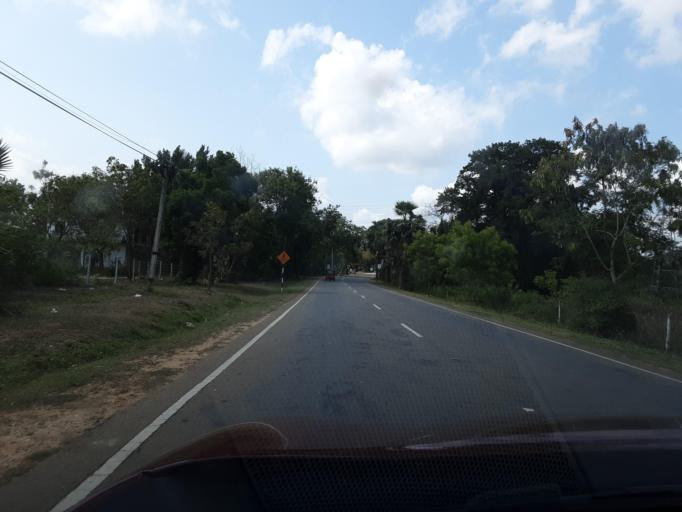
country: LK
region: Southern
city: Tangalla
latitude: 6.2643
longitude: 81.2258
